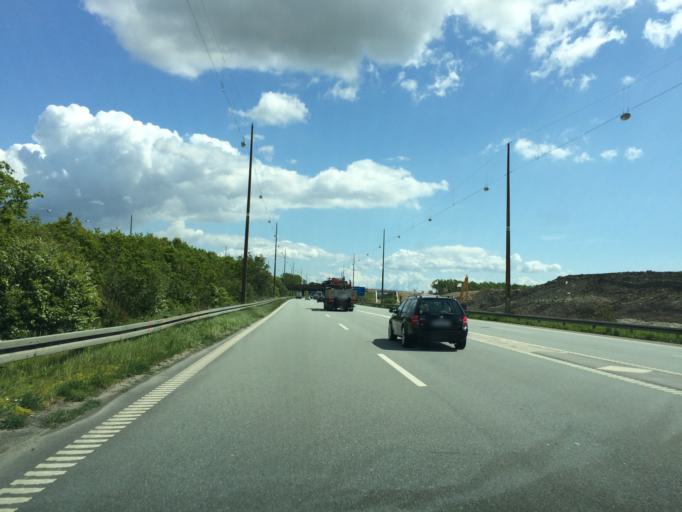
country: DK
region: Capital Region
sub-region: Vallensbaek Kommune
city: Vallensbaek
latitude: 55.6408
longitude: 12.3509
